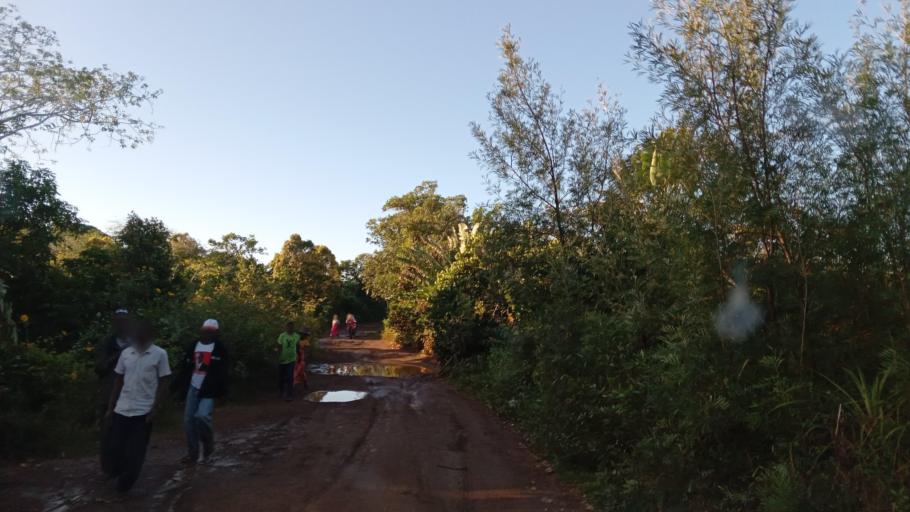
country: MG
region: Atsimo-Atsinanana
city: Vohipaho
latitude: -23.6115
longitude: 47.6093
